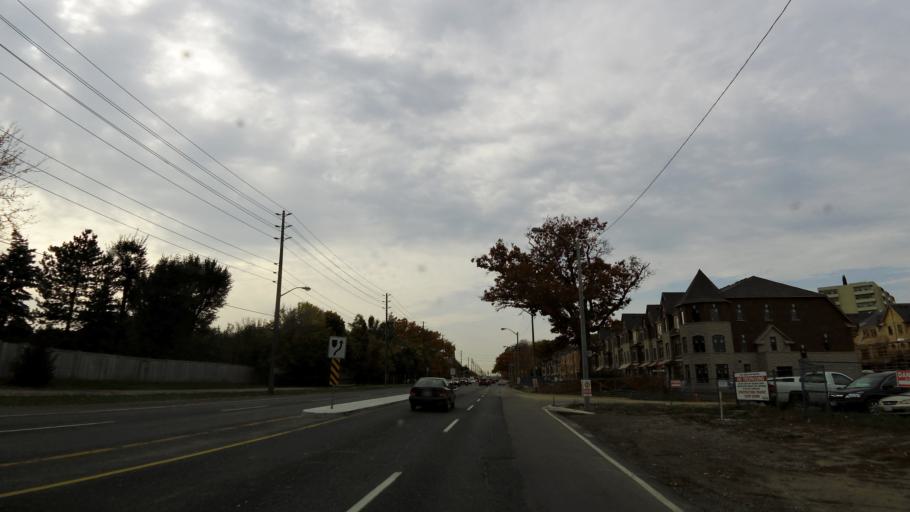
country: CA
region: Ontario
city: Etobicoke
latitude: 43.6780
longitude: -79.5478
